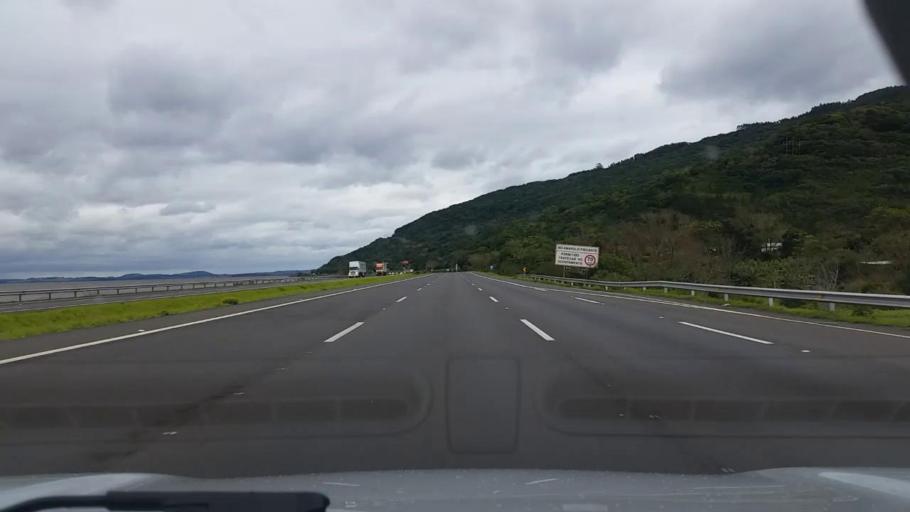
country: BR
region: Rio Grande do Sul
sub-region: Osorio
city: Osorio
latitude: -29.8970
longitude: -50.3251
